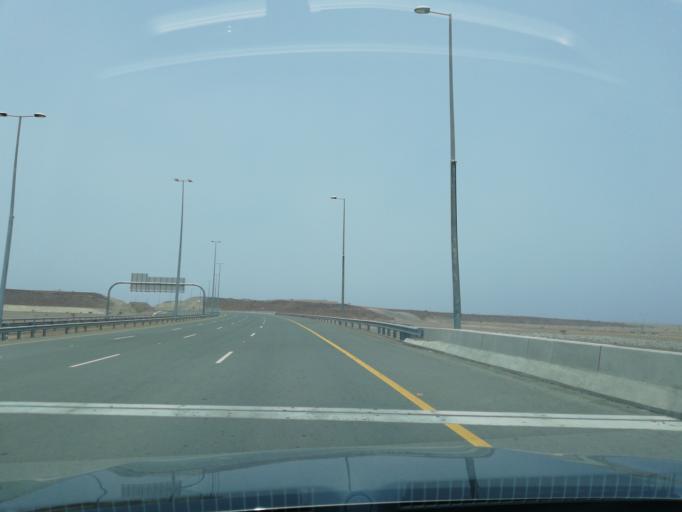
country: OM
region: Al Batinah
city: Al Liwa'
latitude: 24.5365
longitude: 56.4994
